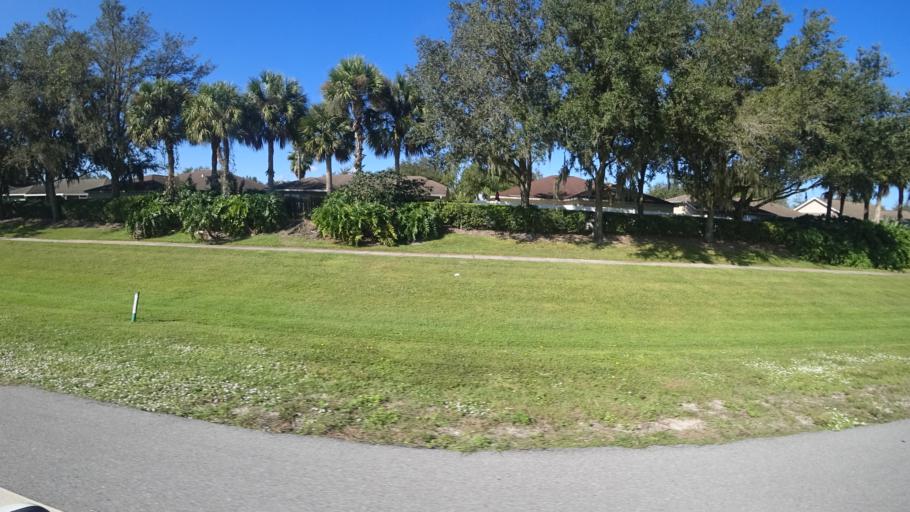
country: US
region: Florida
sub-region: Manatee County
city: Ellenton
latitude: 27.5519
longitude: -82.4254
